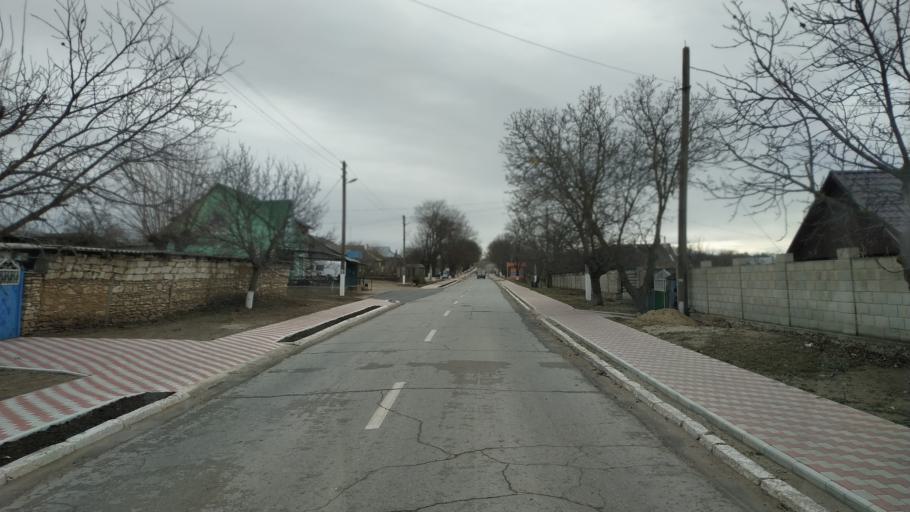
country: MD
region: Telenesti
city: Cocieri
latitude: 47.3407
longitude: 29.0960
